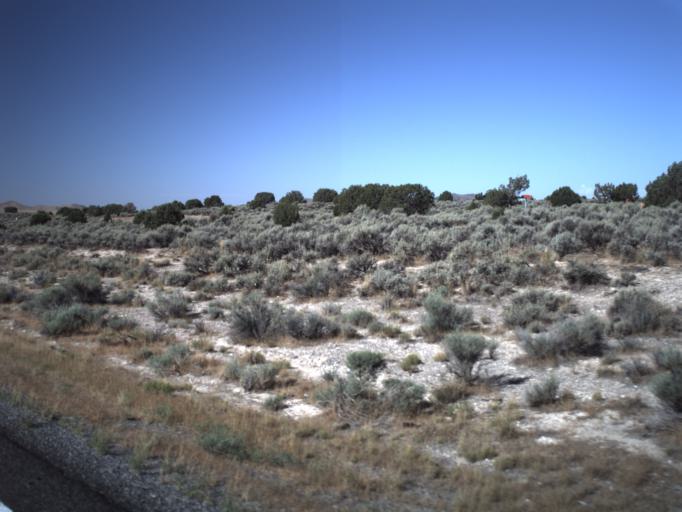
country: US
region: Utah
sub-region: Juab County
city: Mona
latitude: 39.7313
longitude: -112.1935
